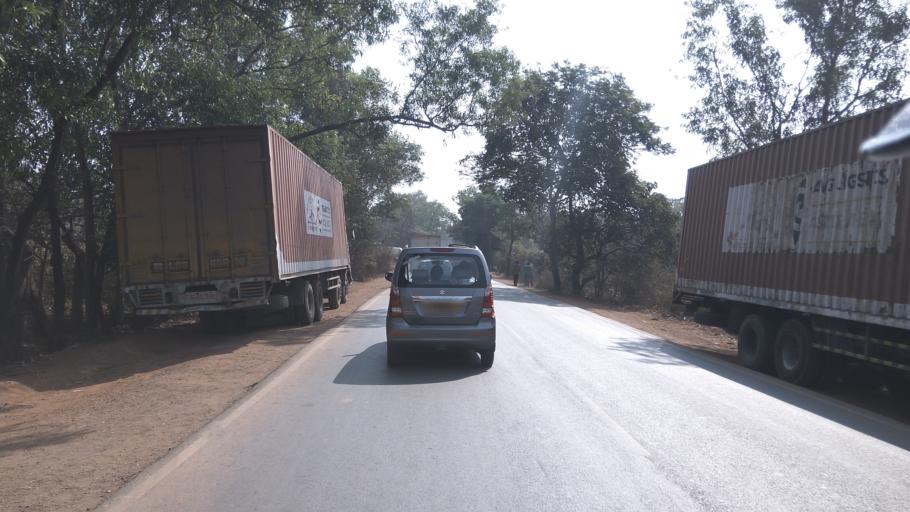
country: IN
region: Goa
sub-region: North Goa
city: Curti
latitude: 15.4181
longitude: 74.0619
